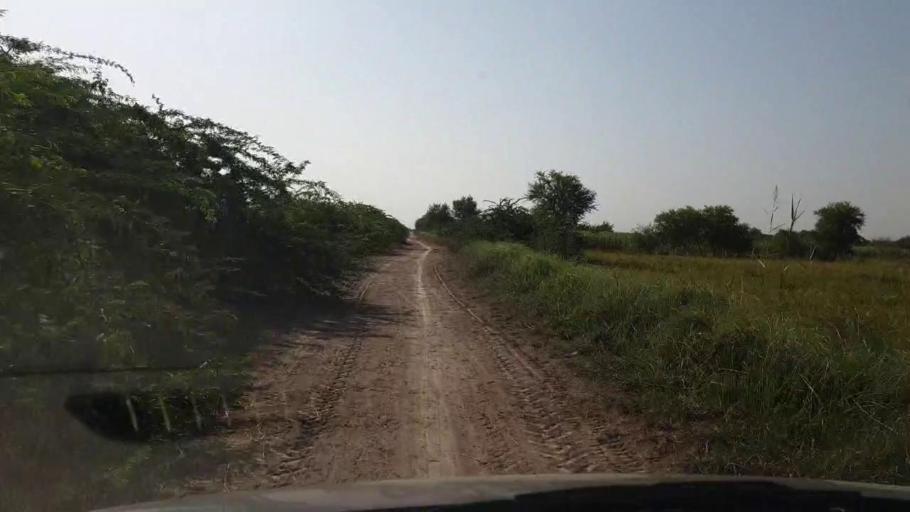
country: PK
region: Sindh
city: Kadhan
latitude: 24.6004
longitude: 69.0748
